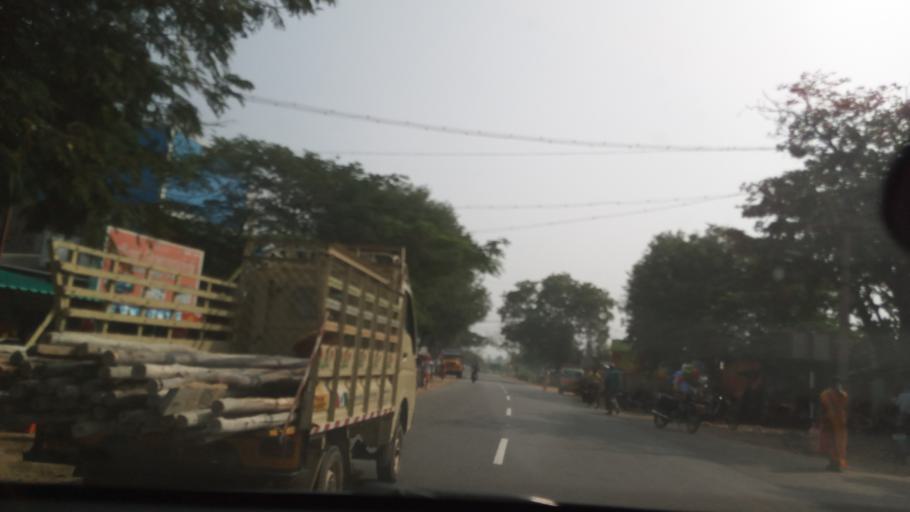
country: IN
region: Tamil Nadu
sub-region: Erode
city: Punjai Puliyampatti
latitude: 11.4037
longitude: 77.1910
